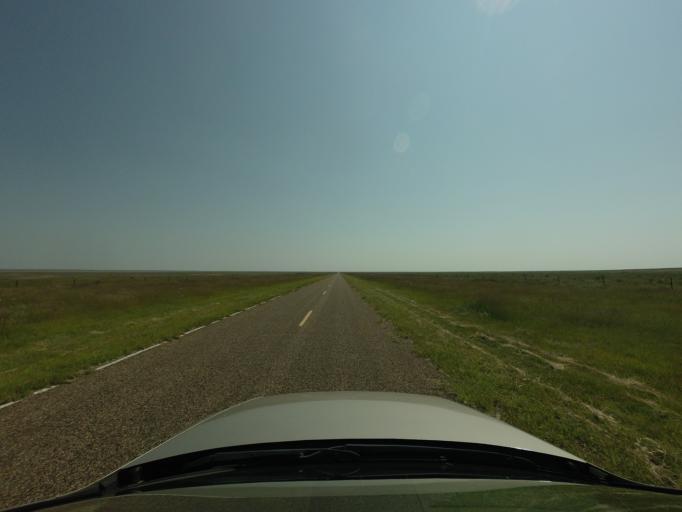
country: US
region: New Mexico
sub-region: Curry County
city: Cannon Air Force Base
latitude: 34.6334
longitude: -103.4867
